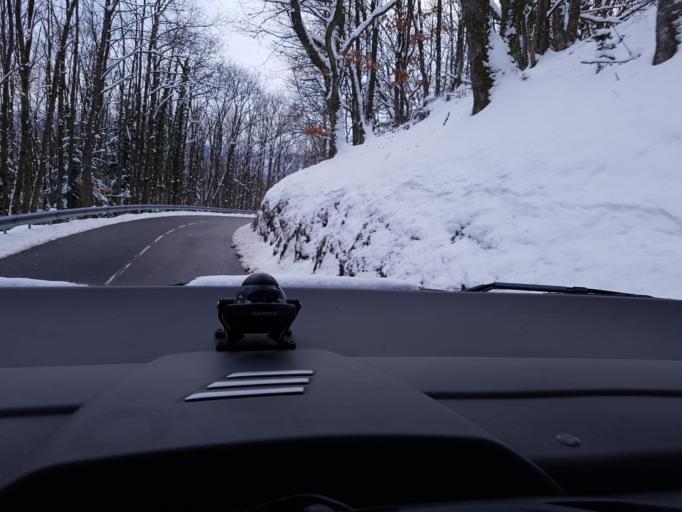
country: FR
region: Alsace
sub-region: Departement du Bas-Rhin
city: Ville
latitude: 48.3707
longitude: 7.2820
